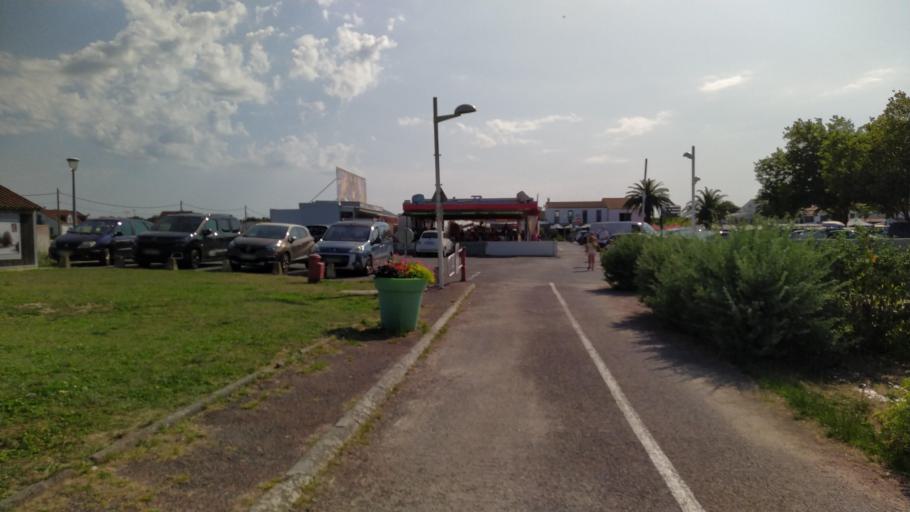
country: FR
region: Poitou-Charentes
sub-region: Departement de la Charente-Maritime
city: Boyard-Ville
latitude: 45.9668
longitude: -1.2411
